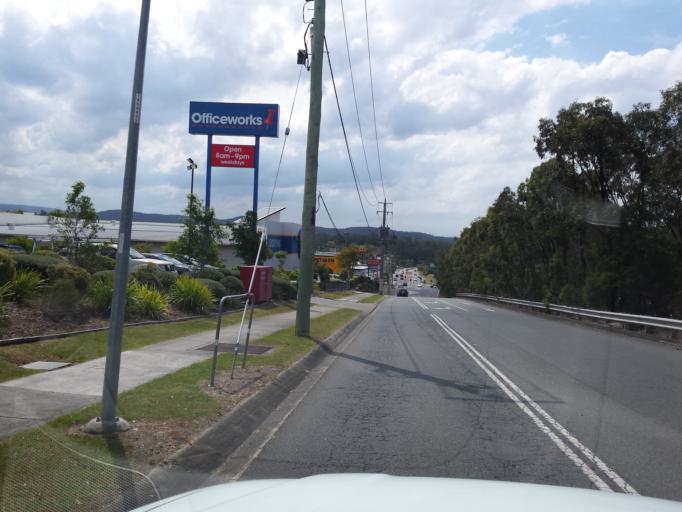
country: AU
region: Queensland
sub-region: Gold Coast
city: Nerang
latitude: -28.0099
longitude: 153.3442
